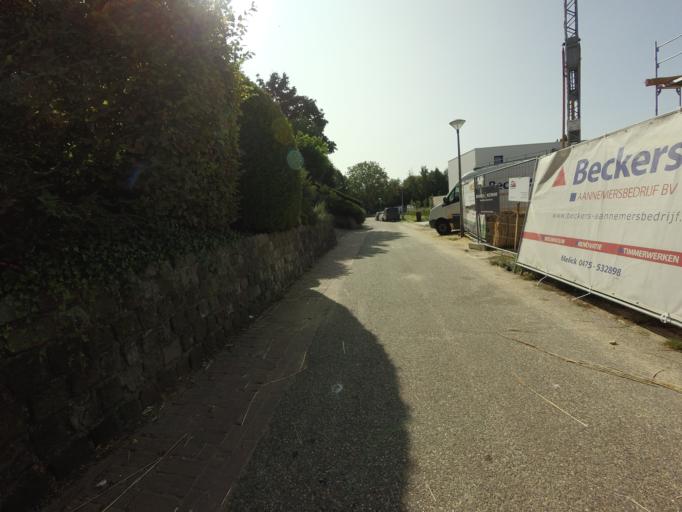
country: NL
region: Limburg
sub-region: Gemeente Roermond
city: Roermond
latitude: 51.1730
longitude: 5.9574
